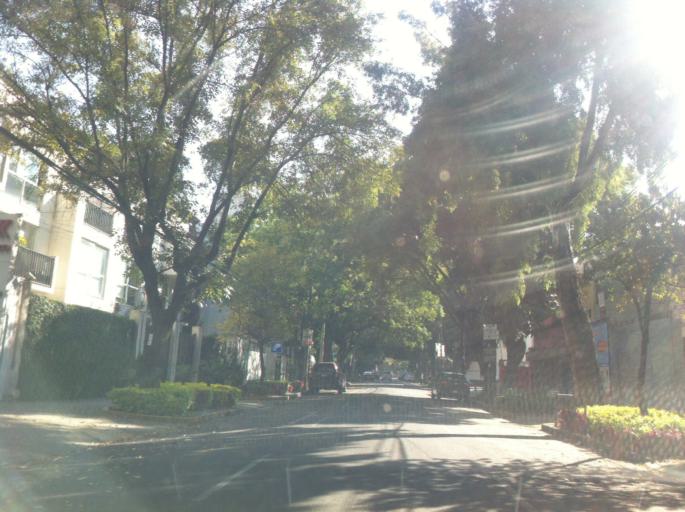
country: MX
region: Mexico City
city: Miguel Hidalgo
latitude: 19.4377
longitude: -99.1937
